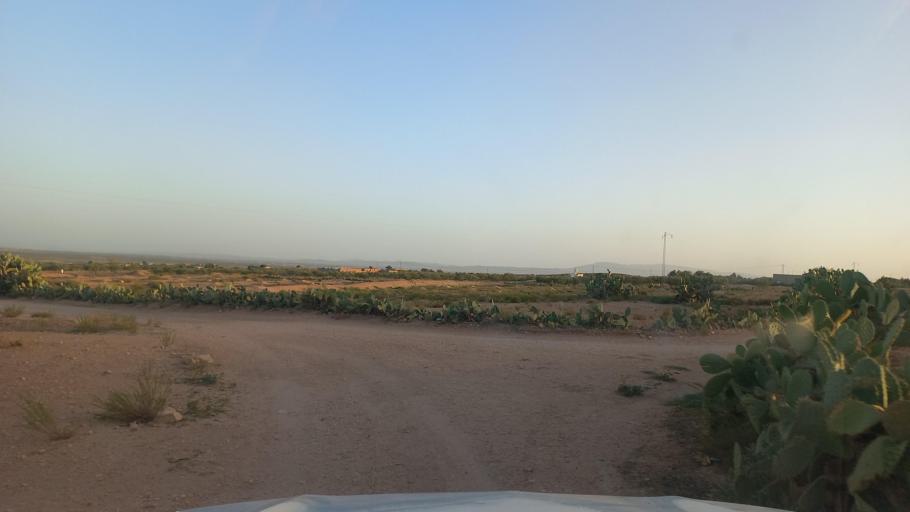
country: TN
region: Al Qasrayn
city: Sbiba
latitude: 35.3747
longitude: 9.0102
